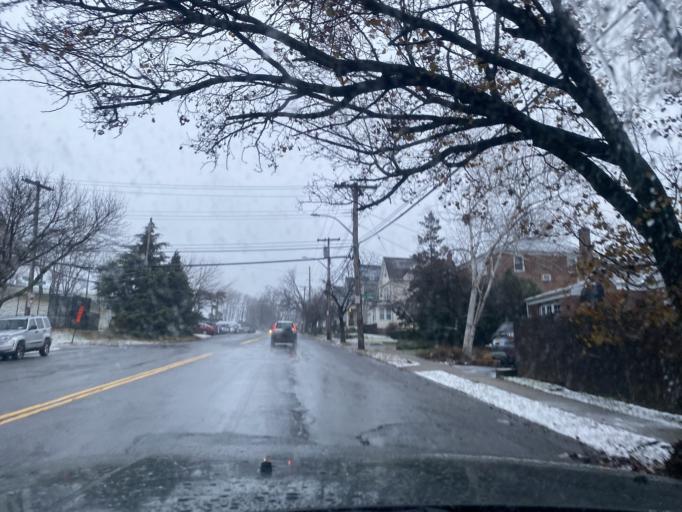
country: US
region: New York
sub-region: Westchester County
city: Mount Vernon
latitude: 40.9055
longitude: -73.8673
